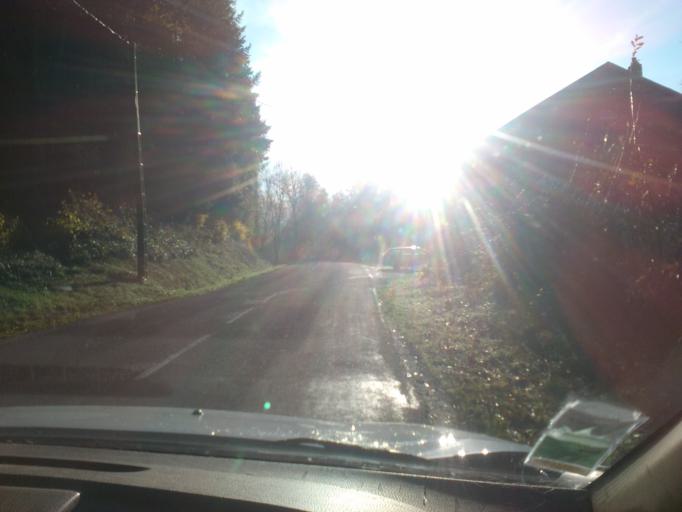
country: FR
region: Lorraine
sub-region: Departement des Vosges
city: Uzemain
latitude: 48.0675
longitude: 6.3181
